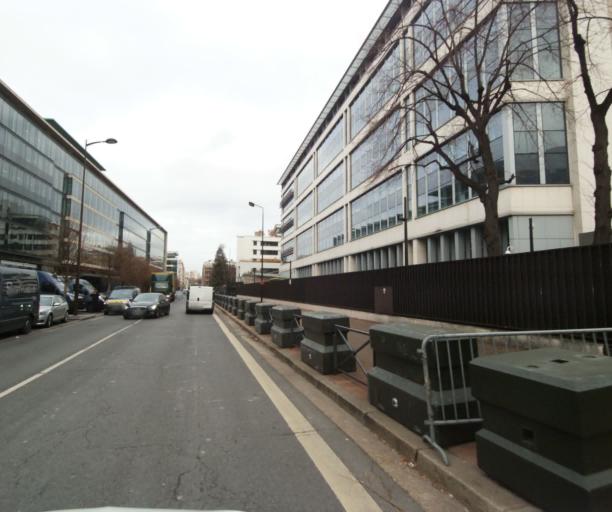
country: FR
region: Ile-de-France
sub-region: Departement des Hauts-de-Seine
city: Levallois-Perret
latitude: 48.8919
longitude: 2.2779
